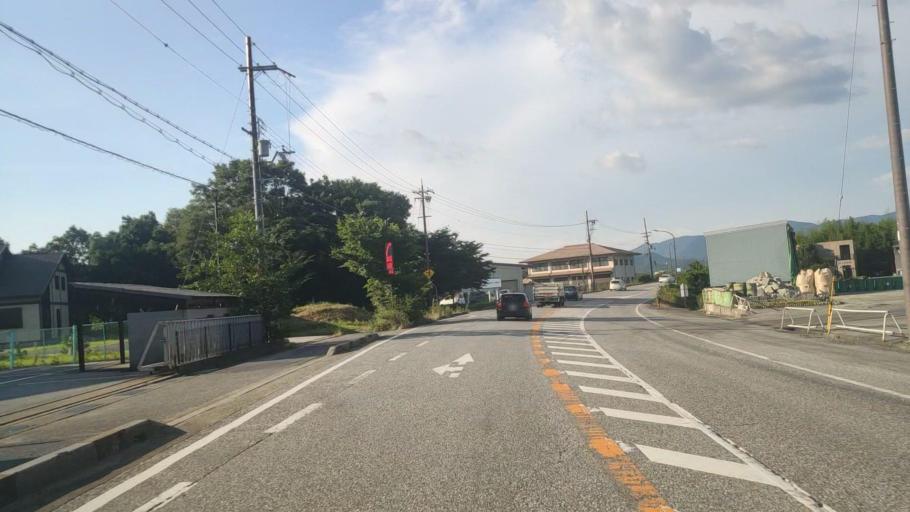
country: JP
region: Shiga Prefecture
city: Hikone
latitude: 35.2054
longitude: 136.2758
